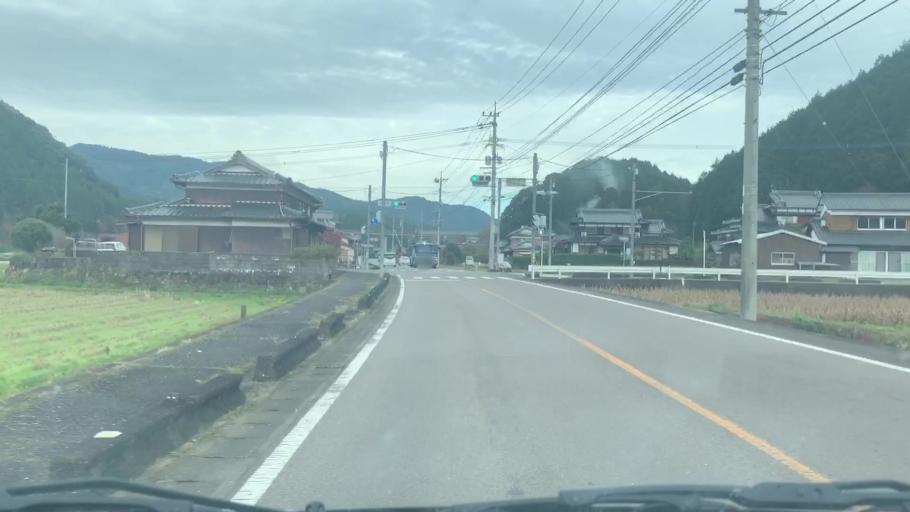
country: JP
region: Saga Prefecture
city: Ureshinomachi-shimojuku
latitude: 33.1396
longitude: 129.9786
